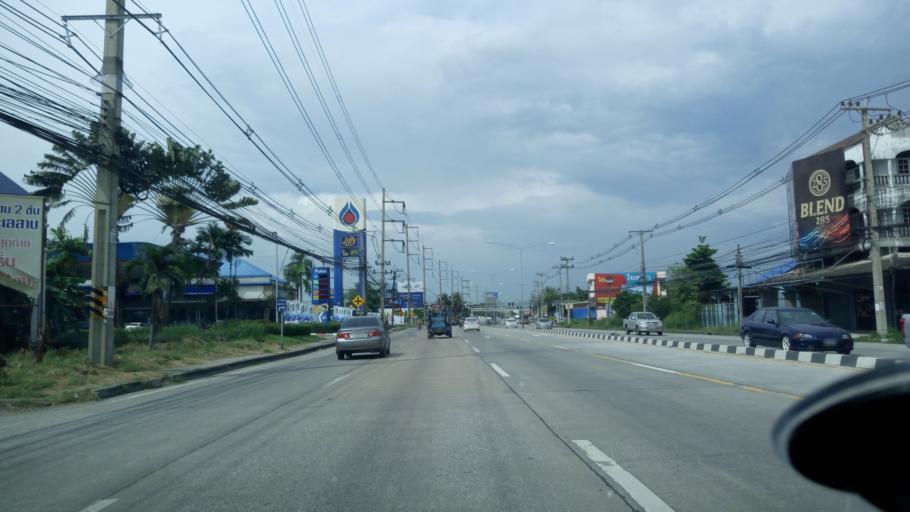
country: TH
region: Chon Buri
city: Chon Buri
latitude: 13.3997
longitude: 101.0283
